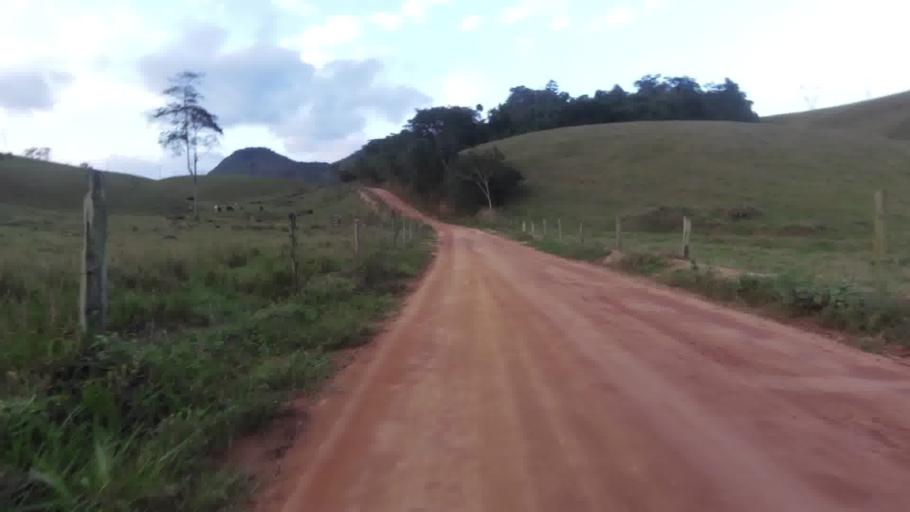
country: BR
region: Espirito Santo
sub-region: Guarapari
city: Guarapari
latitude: -20.6703
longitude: -40.6115
